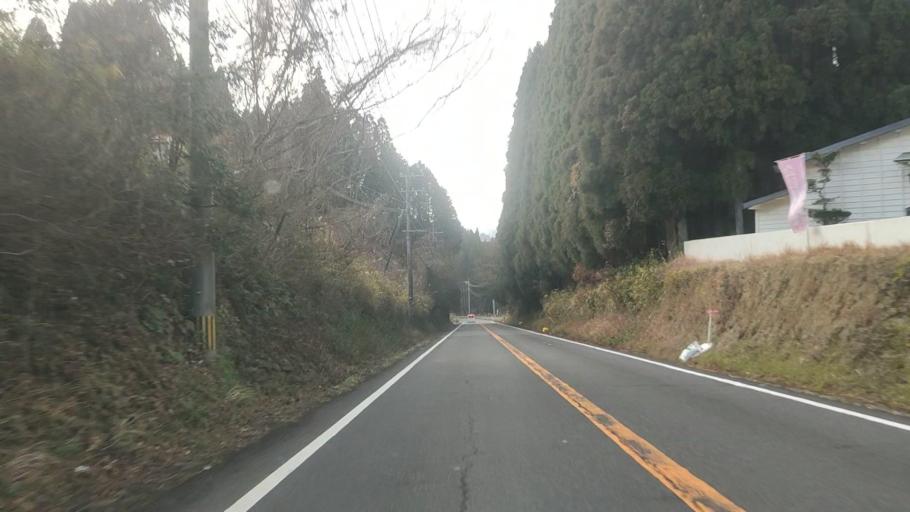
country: JP
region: Kagoshima
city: Okuchi-shinohara
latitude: 31.9239
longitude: 130.7001
